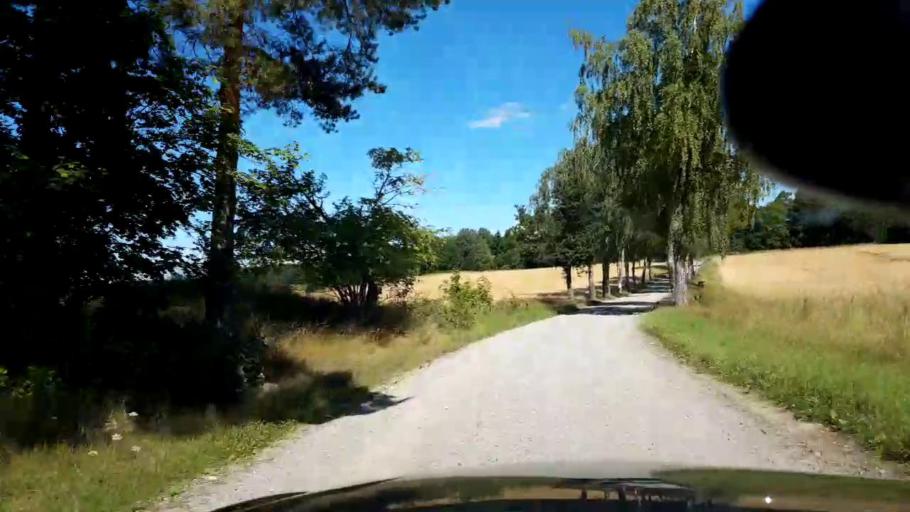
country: SE
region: Stockholm
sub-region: Sigtuna Kommun
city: Sigtuna
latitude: 59.6119
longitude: 17.6370
